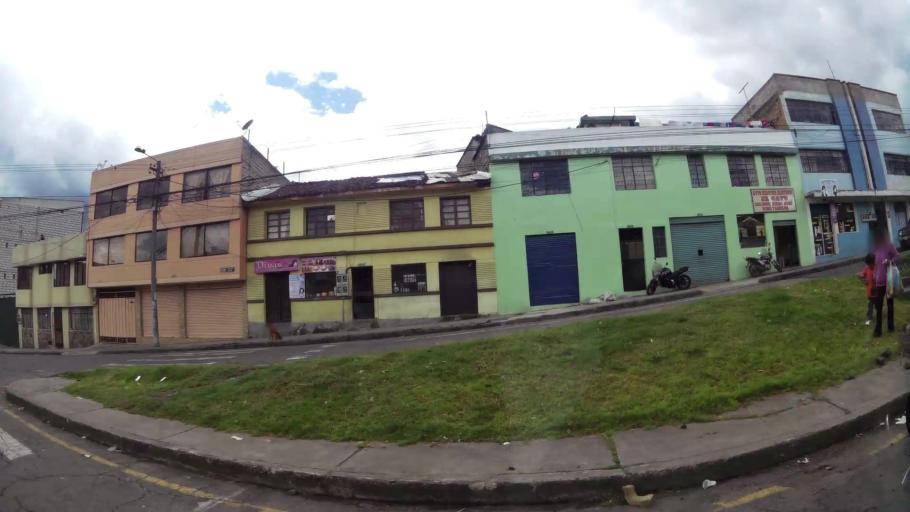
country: EC
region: Pichincha
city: Quito
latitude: -0.2495
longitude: -78.5160
